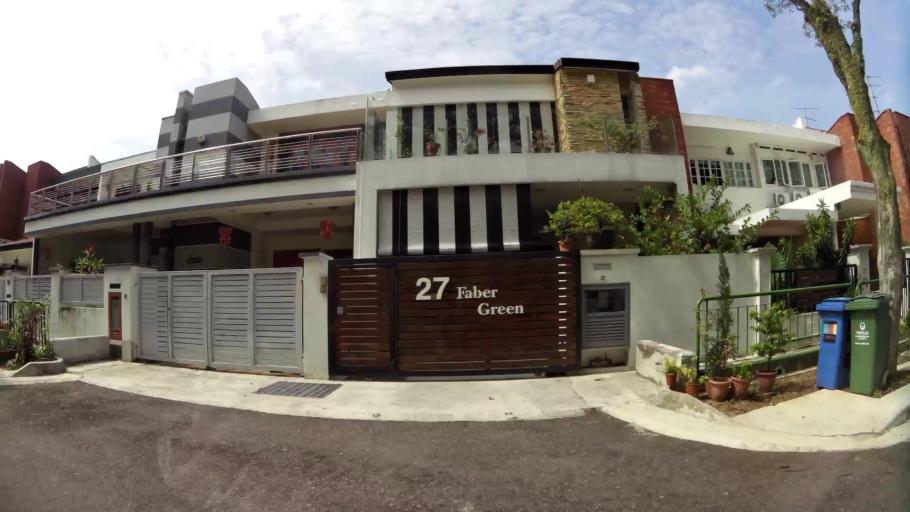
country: SG
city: Singapore
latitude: 1.3197
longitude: 103.7573
